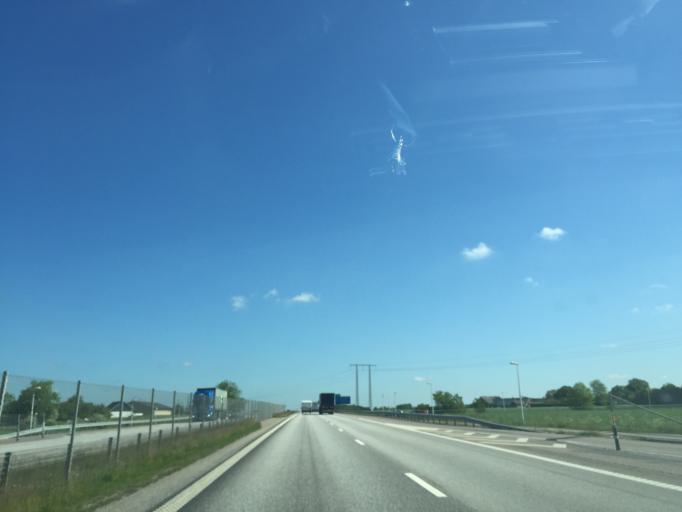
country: SE
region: Skane
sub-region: Astorps Kommun
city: Astorp
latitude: 56.1353
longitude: 12.9225
